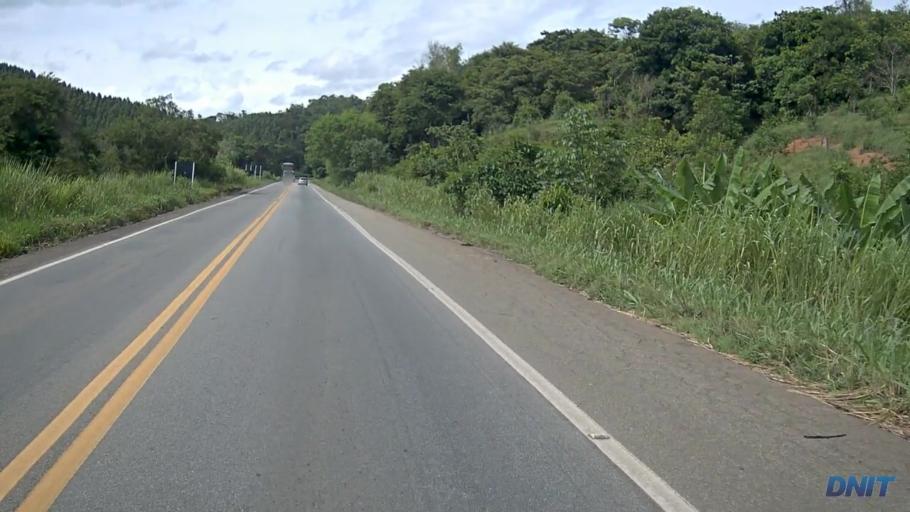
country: BR
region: Minas Gerais
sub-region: Ipaba
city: Ipaba
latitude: -19.3292
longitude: -42.4201
